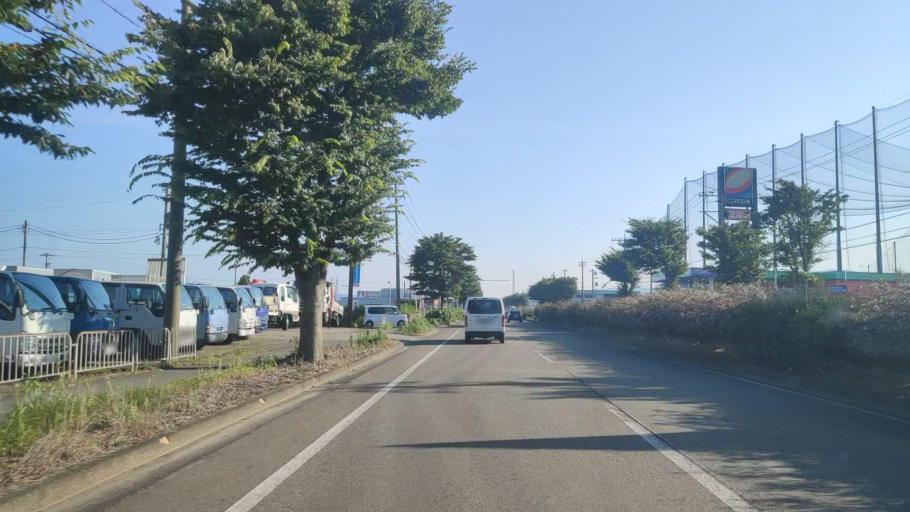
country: JP
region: Fukui
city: Maruoka
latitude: 36.1302
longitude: 136.2611
